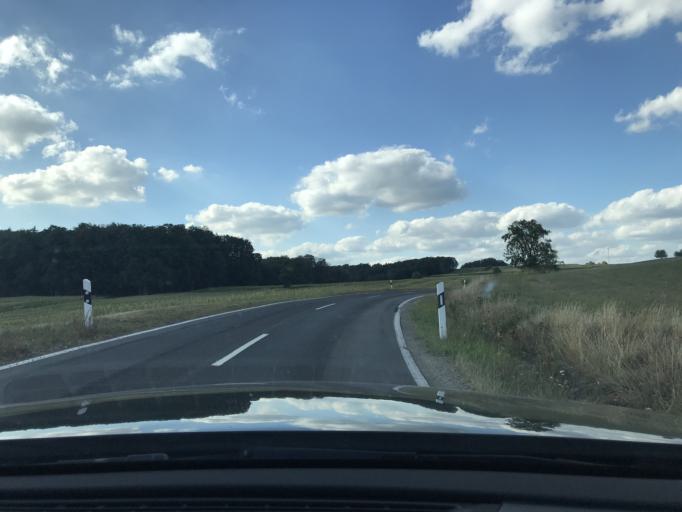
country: DE
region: Bavaria
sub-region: Regierungsbezirk Unterfranken
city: Kirchlauter
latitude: 50.0661
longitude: 10.6697
